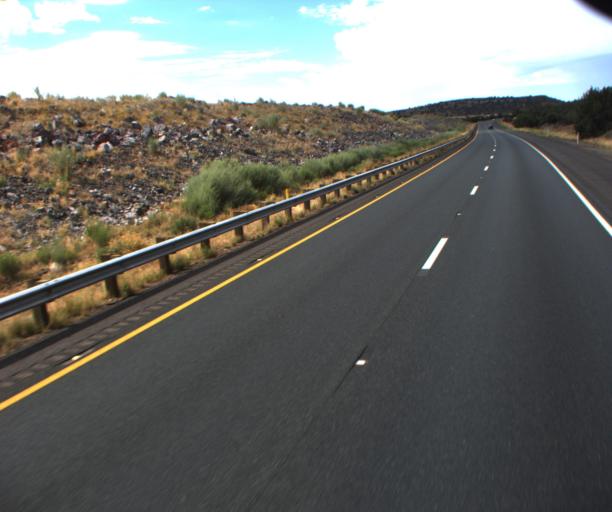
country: US
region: Arizona
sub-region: Yavapai County
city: Camp Verde
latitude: 34.4984
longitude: -112.0045
